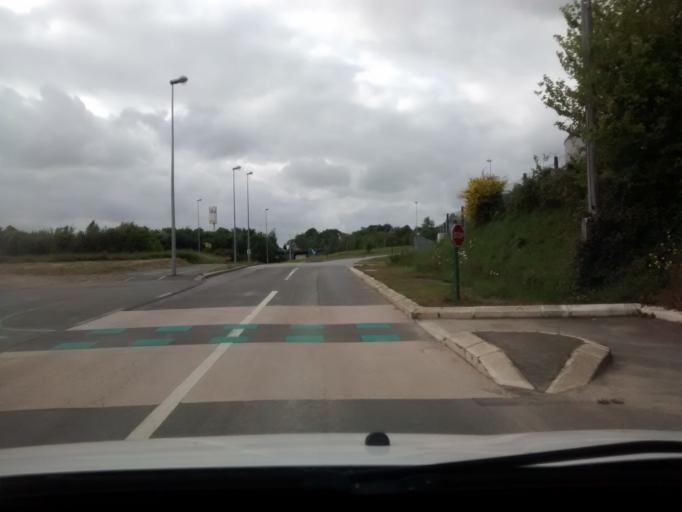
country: FR
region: Brittany
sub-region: Departement d'Ille-et-Vilaine
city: Cesson-Sevigne
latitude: 48.1099
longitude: -1.5842
